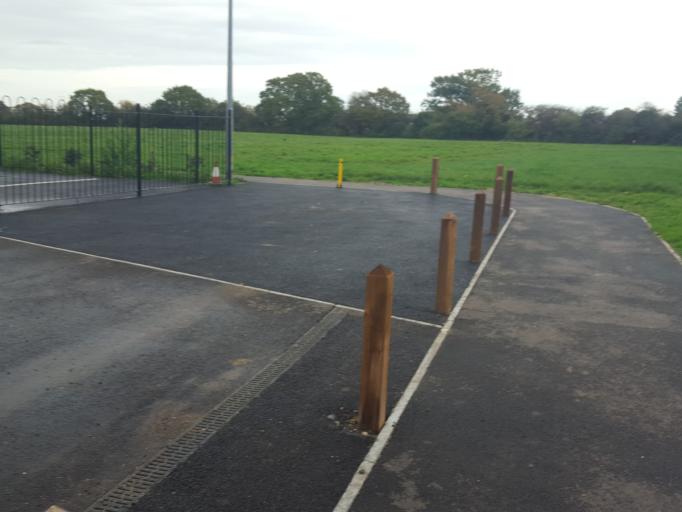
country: GB
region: England
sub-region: Essex
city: Little Clacton
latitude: 51.8180
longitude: 1.1552
